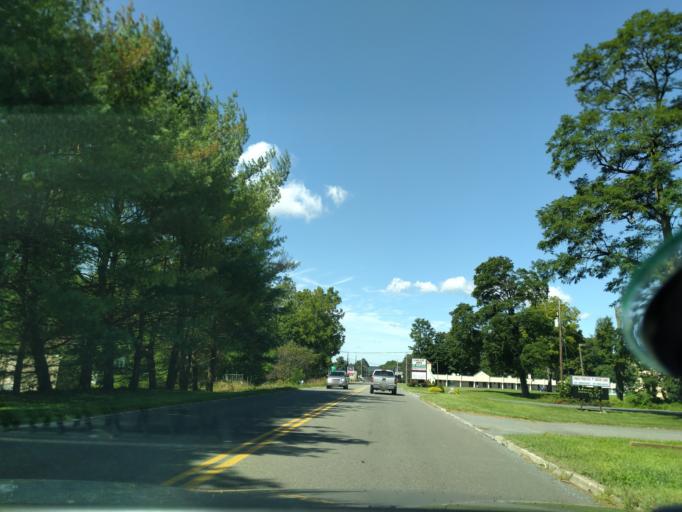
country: US
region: Pennsylvania
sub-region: Pike County
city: Saw Creek
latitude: 41.0649
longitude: -75.0582
